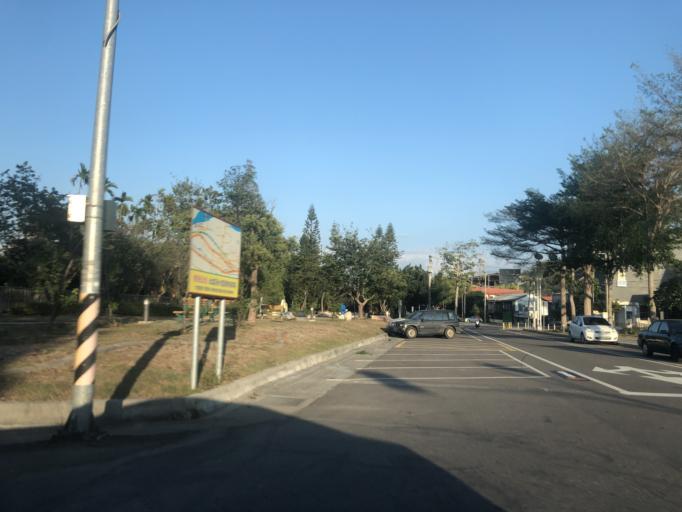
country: TW
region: Taiwan
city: Fengyuan
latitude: 24.2754
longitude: 120.7796
